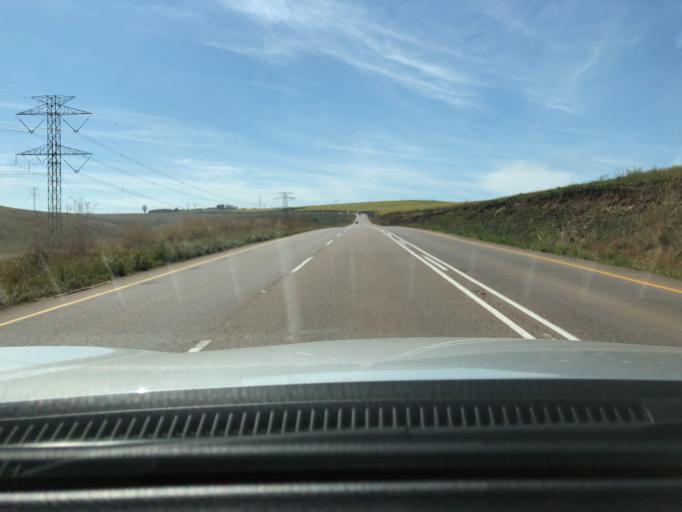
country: ZA
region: KwaZulu-Natal
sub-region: uMgungundlovu District Municipality
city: Richmond
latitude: -29.7642
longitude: 30.3684
